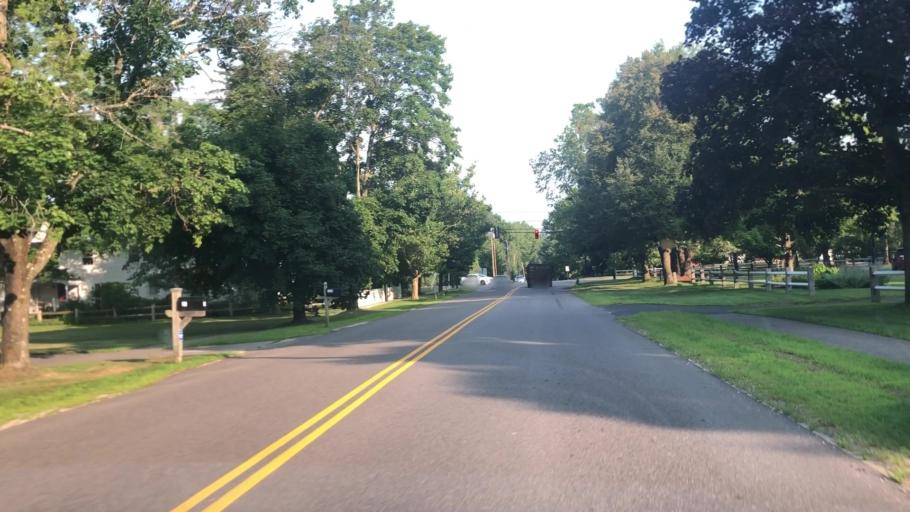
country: US
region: New Hampshire
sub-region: Hillsborough County
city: Milford
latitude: 42.8620
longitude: -71.6262
